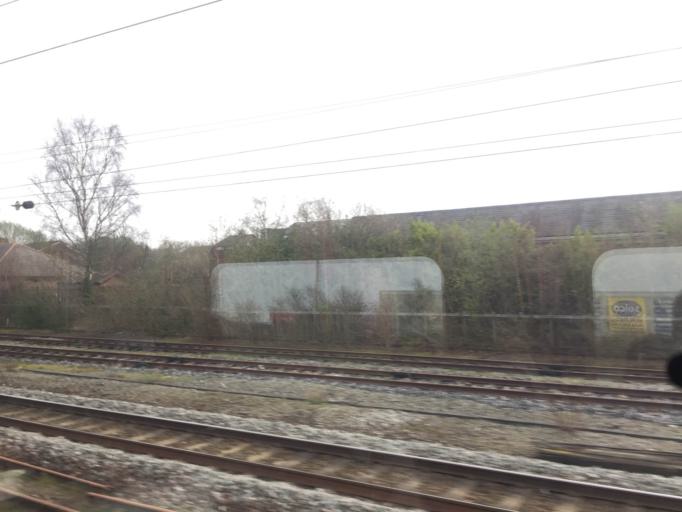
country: GB
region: England
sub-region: Warrington
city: Warrington
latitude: 53.3895
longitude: -2.6040
